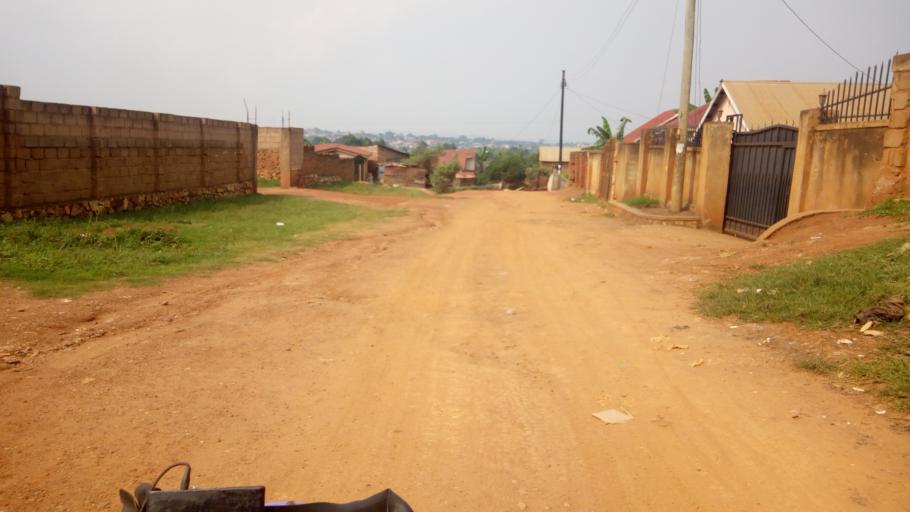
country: UG
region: Central Region
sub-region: Wakiso District
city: Kireka
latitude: 0.3242
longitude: 32.6546
